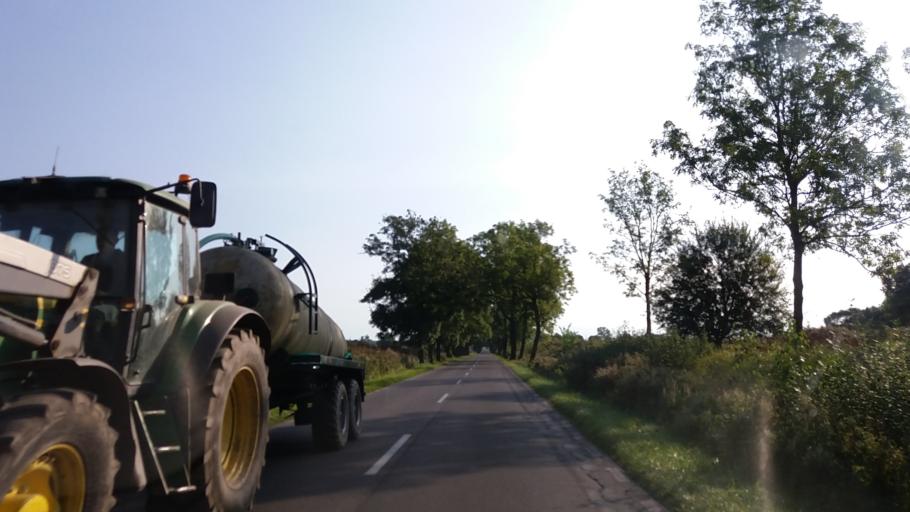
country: PL
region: West Pomeranian Voivodeship
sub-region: Powiat choszczenski
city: Choszczno
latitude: 53.1748
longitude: 15.4847
